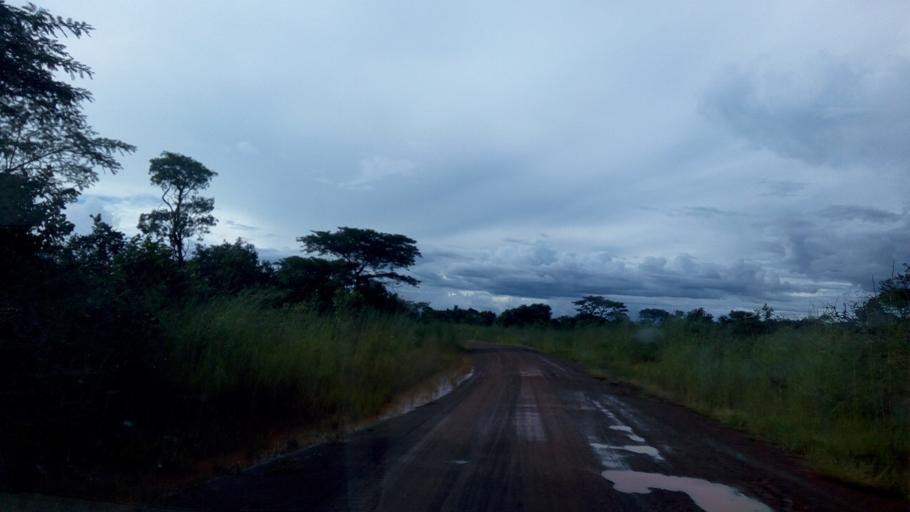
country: ZM
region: Luapula
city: Mwense
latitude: -10.4121
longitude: 28.1187
